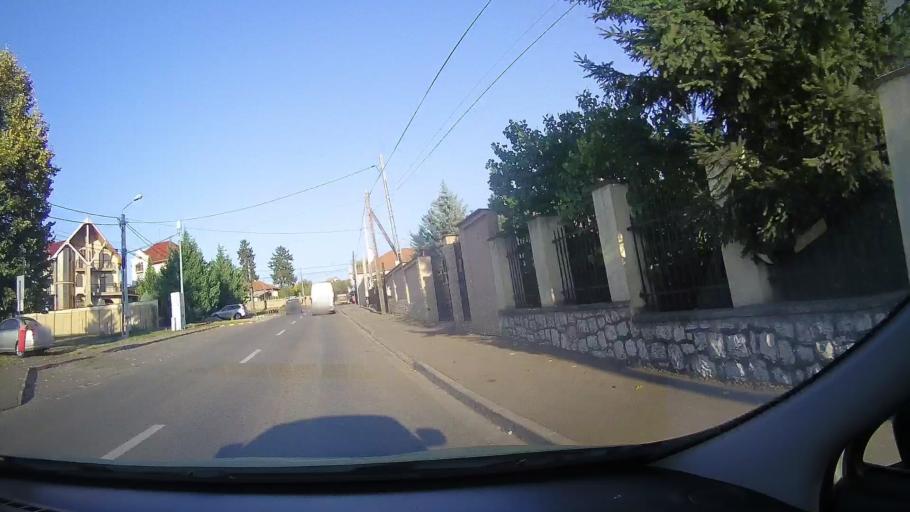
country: RO
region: Bihor
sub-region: Comuna Biharea
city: Oradea
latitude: 47.0888
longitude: 21.9253
